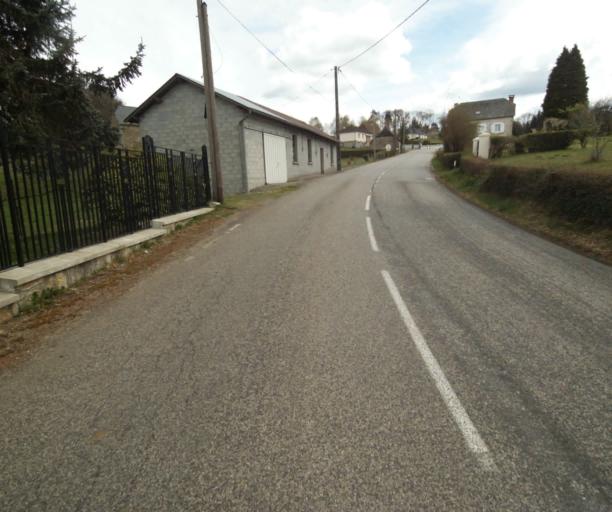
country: FR
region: Limousin
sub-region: Departement de la Correze
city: Laguenne
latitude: 45.2115
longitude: 1.8662
